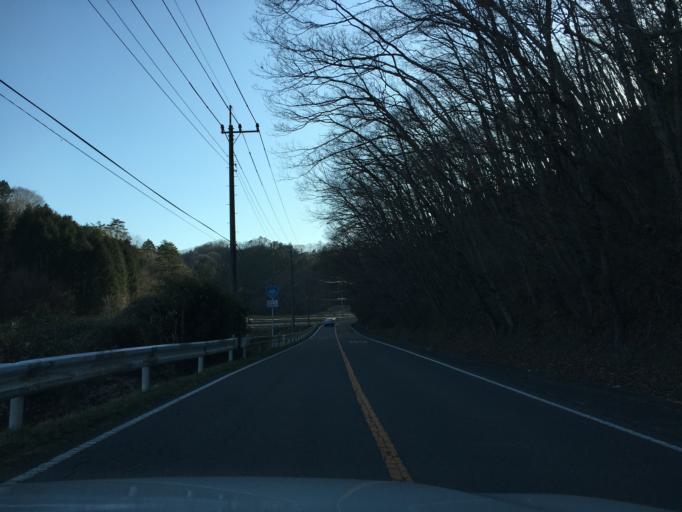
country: JP
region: Ibaraki
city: Daigo
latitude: 36.7757
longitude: 140.2628
